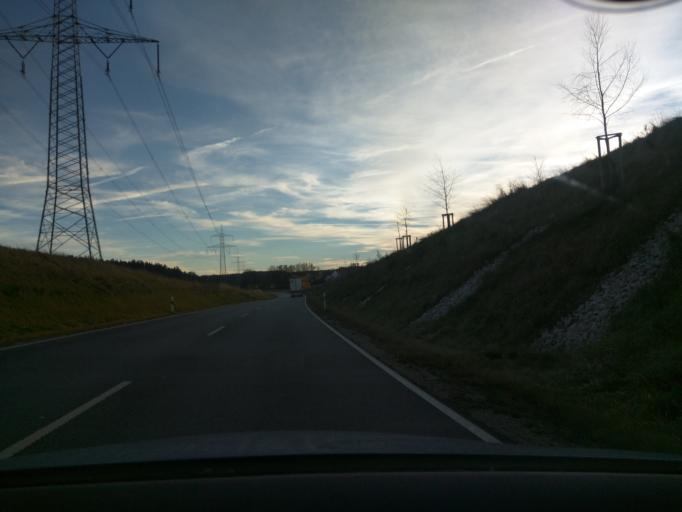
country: DE
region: Bavaria
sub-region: Upper Bavaria
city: Au in der Hallertau
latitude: 48.5537
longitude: 11.7286
